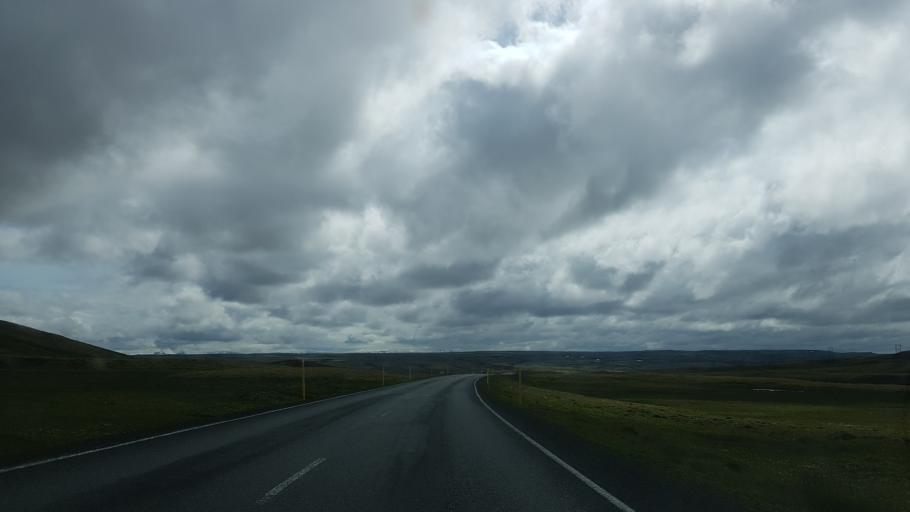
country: IS
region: West
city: Borgarnes
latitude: 64.9626
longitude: -21.0608
